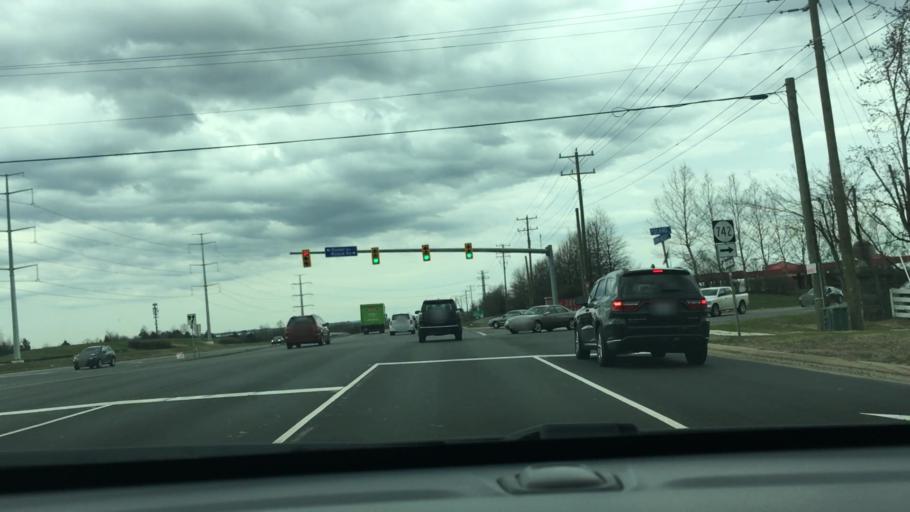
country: US
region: Virginia
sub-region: Loudoun County
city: South Riding
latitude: 38.9208
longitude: -77.4976
